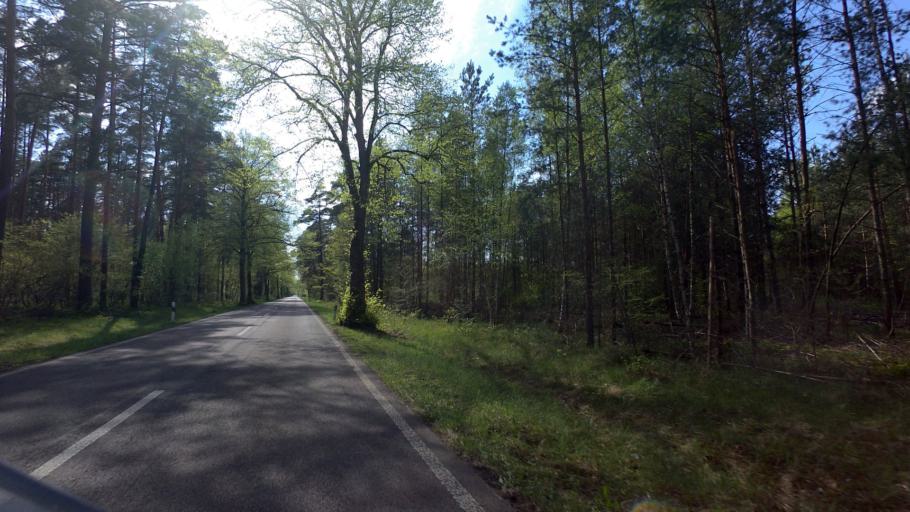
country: DE
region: Brandenburg
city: Milmersdorf
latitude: 53.0016
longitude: 13.5743
